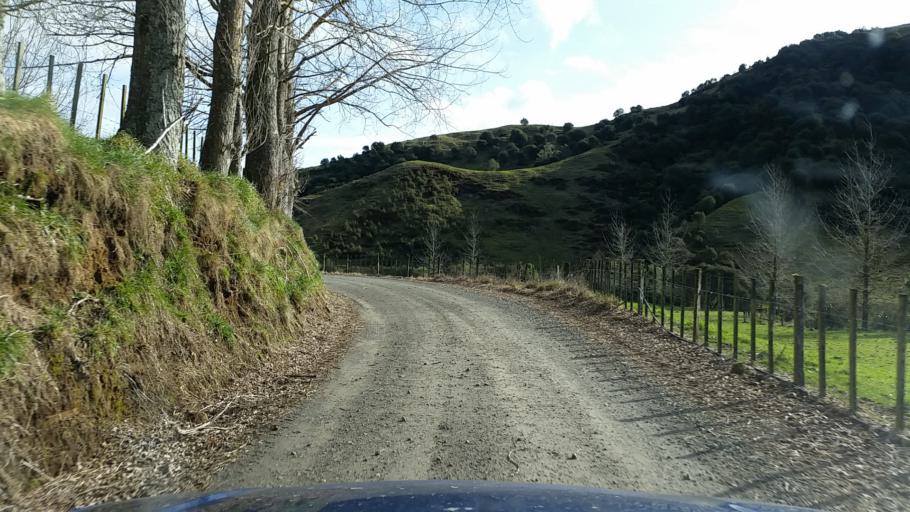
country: NZ
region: Taranaki
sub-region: South Taranaki District
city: Eltham
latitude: -39.2603
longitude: 174.5853
